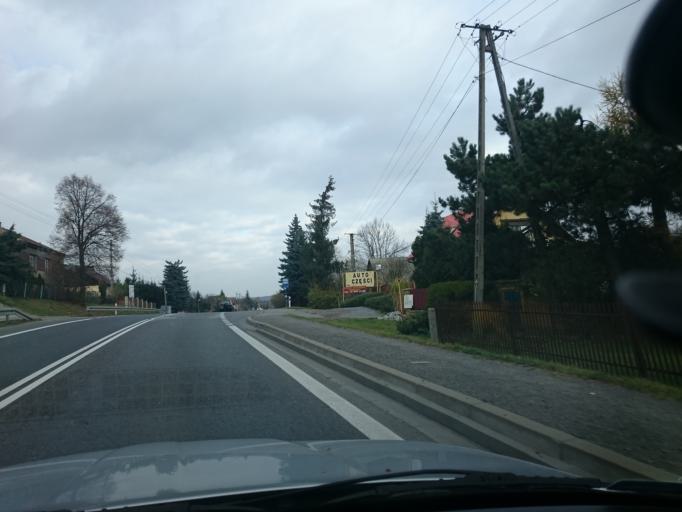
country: PL
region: Lesser Poland Voivodeship
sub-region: Powiat krakowski
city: Michalowice
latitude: 50.1676
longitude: 19.9780
